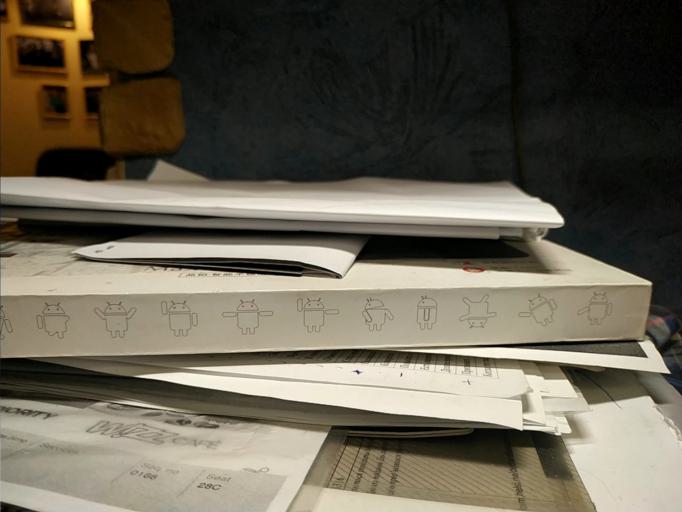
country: RU
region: Tverskaya
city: Zubtsov
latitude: 56.0833
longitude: 34.7846
